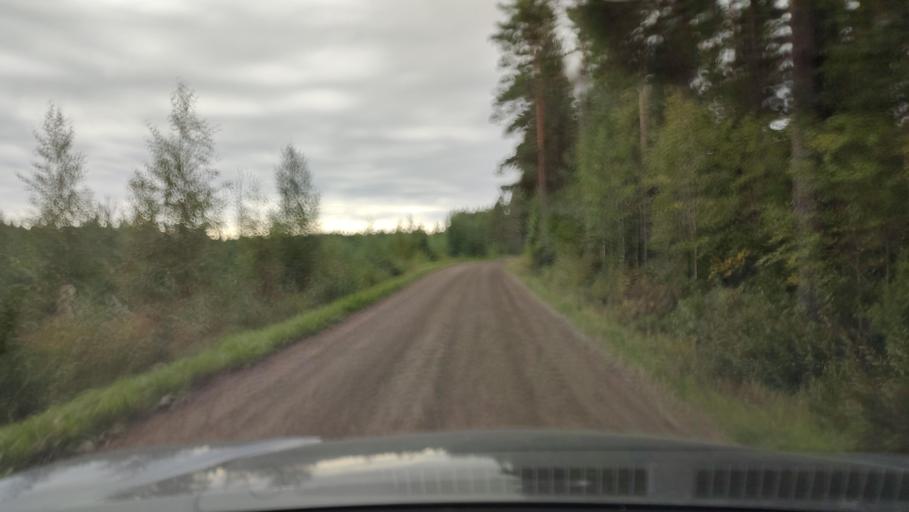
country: FI
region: Southern Ostrobothnia
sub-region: Suupohja
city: Karijoki
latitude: 62.2231
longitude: 21.5722
